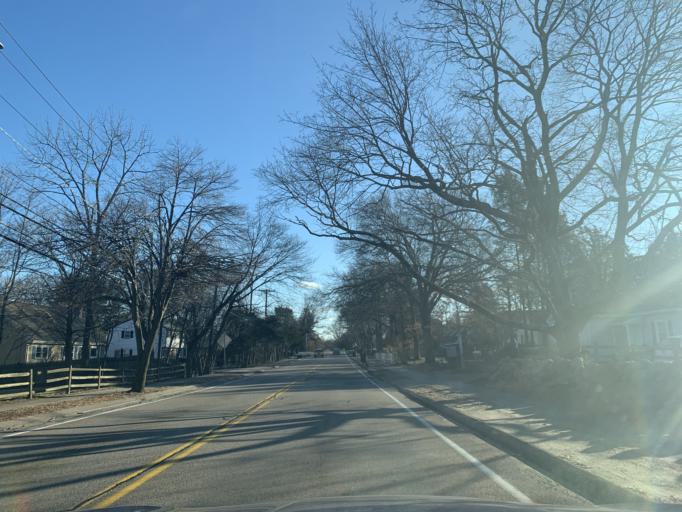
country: US
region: Massachusetts
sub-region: Norfolk County
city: Norwood
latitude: 42.1835
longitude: -71.1820
